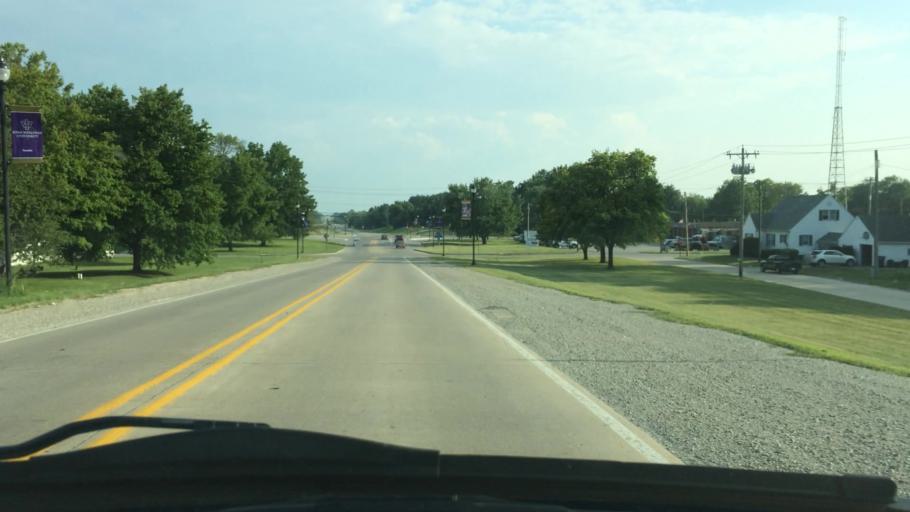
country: US
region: Iowa
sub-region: Henry County
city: Mount Pleasant
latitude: 40.9663
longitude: -91.5391
